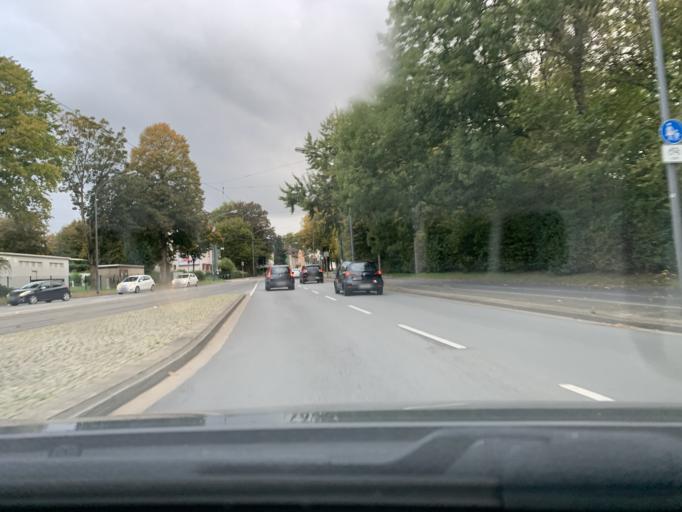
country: DE
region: North Rhine-Westphalia
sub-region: Regierungsbezirk Dusseldorf
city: Oberhausen
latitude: 51.4632
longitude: 6.9322
